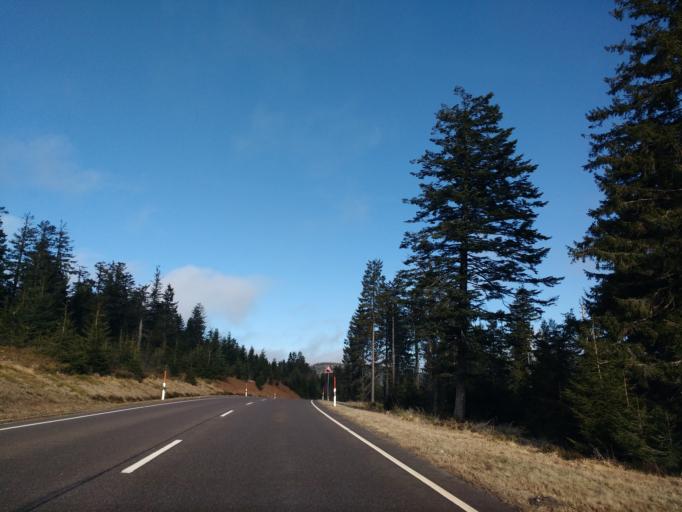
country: DE
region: Baden-Wuerttemberg
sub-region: Freiburg Region
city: Seebach
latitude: 48.5529
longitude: 8.2158
